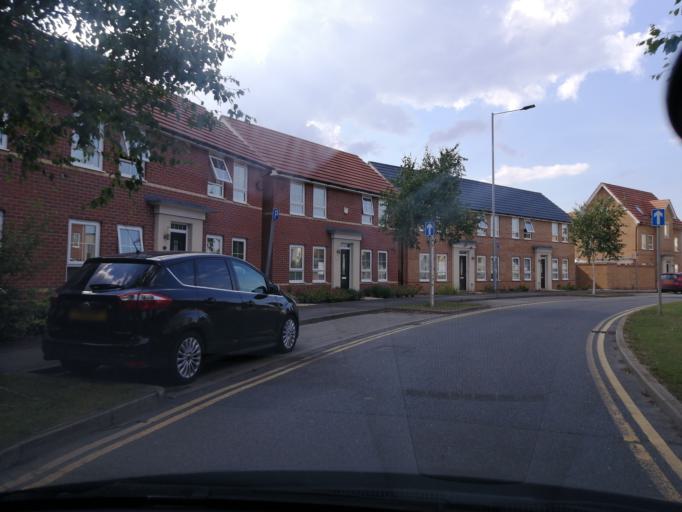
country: GB
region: England
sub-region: Peterborough
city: Peterborough
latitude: 52.5500
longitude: -0.2504
